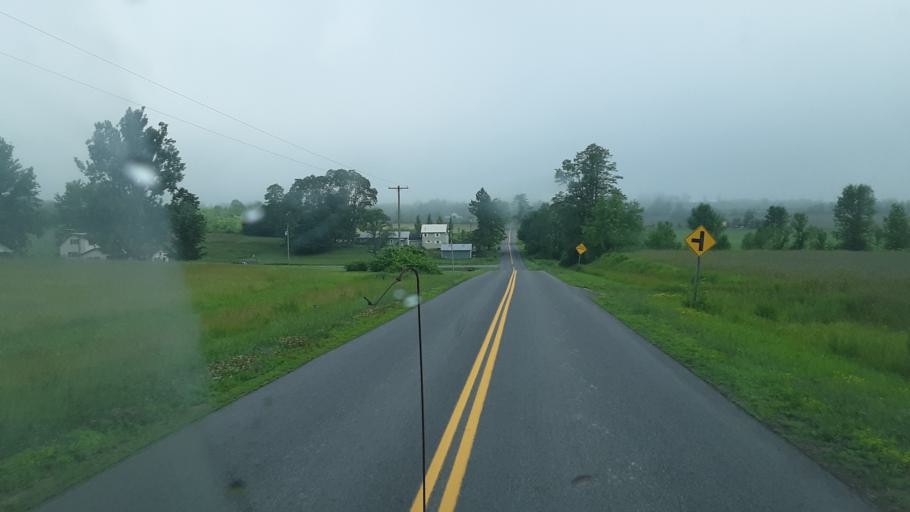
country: US
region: New York
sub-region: Montgomery County
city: Fonda
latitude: 42.9143
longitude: -74.3771
